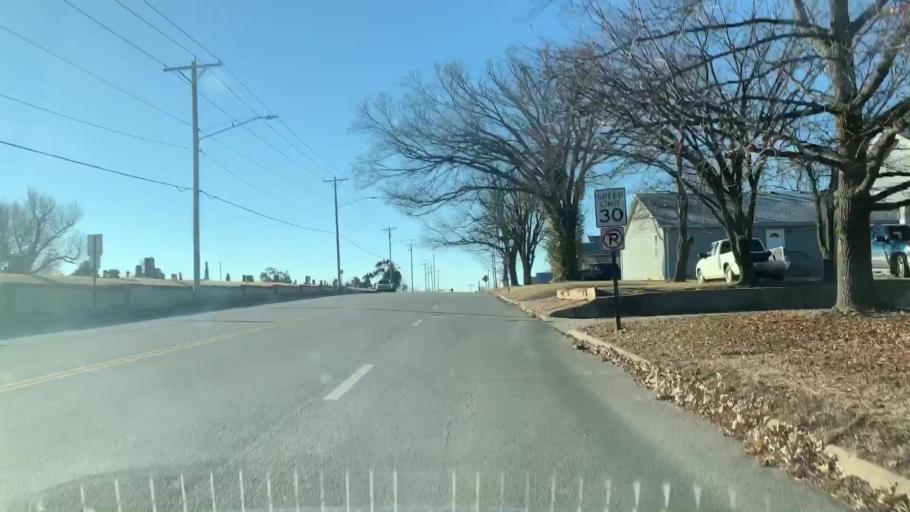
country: US
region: Kansas
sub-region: Crawford County
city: Pittsburg
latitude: 37.3850
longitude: -94.7053
